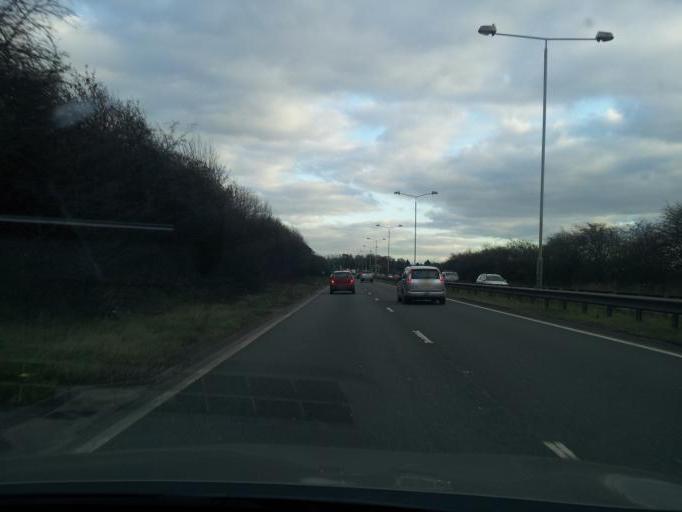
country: GB
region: England
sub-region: Nottinghamshire
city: Ruddington
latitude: 52.9105
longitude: -1.1529
